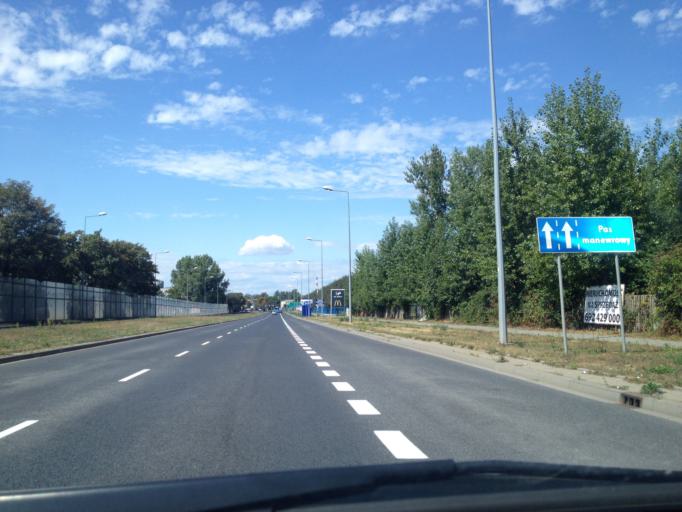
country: PL
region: Lower Silesian Voivodeship
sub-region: Legnica
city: Legnica
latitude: 51.1763
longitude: 16.1651
